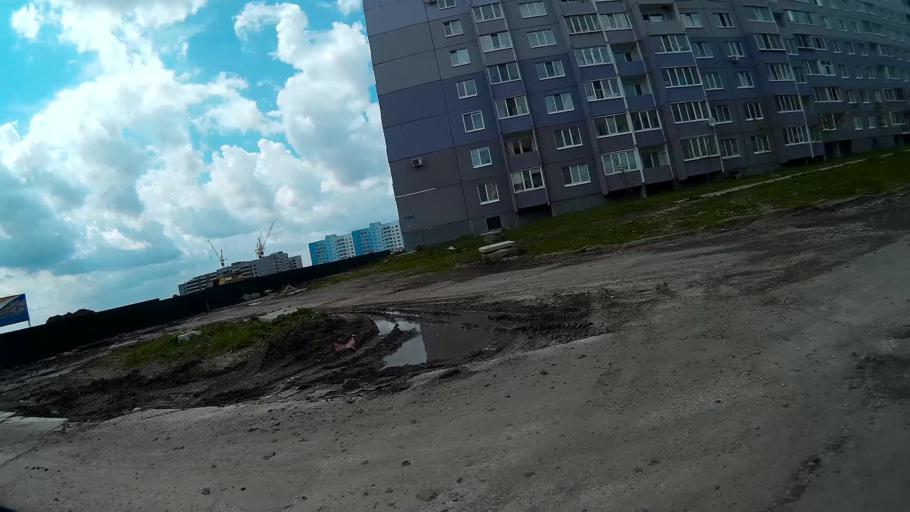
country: RU
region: Ulyanovsk
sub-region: Ulyanovskiy Rayon
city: Ulyanovsk
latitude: 54.3471
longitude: 48.3421
